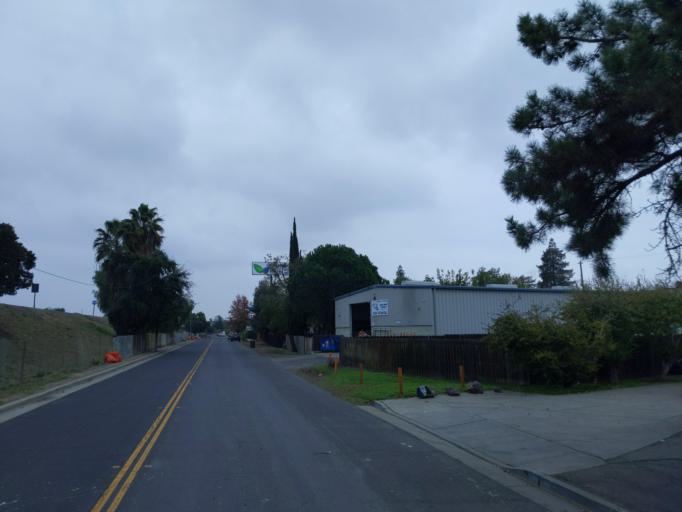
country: US
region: California
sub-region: San Joaquin County
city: Country Club
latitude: 37.9556
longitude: -121.3208
